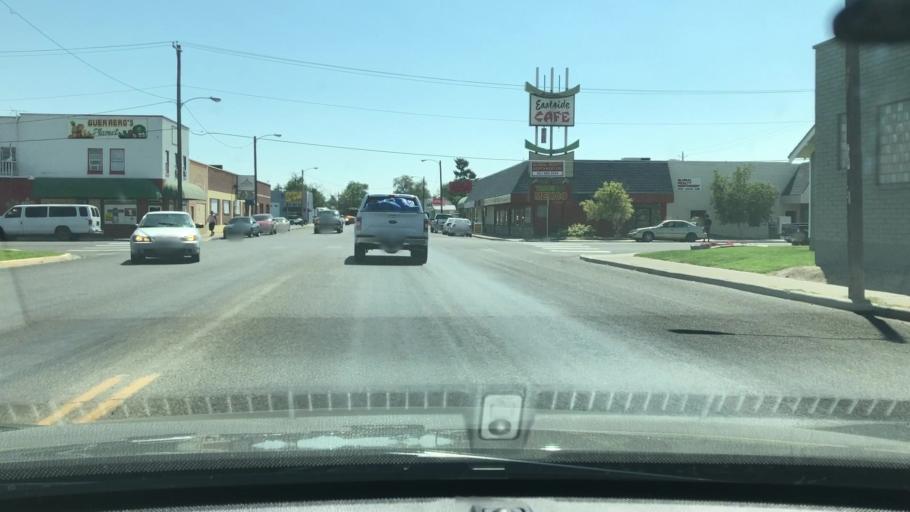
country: US
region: Oregon
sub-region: Malheur County
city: Ontario
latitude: 44.0255
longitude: -116.9589
